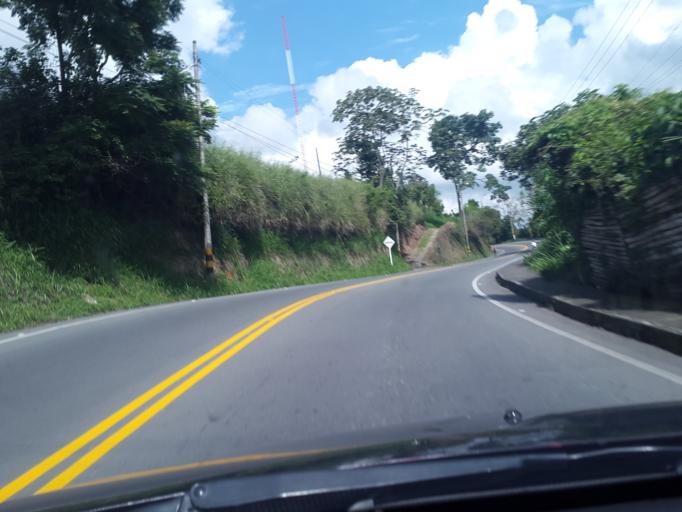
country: CO
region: Quindio
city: Calarca
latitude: 4.5350
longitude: -75.6469
